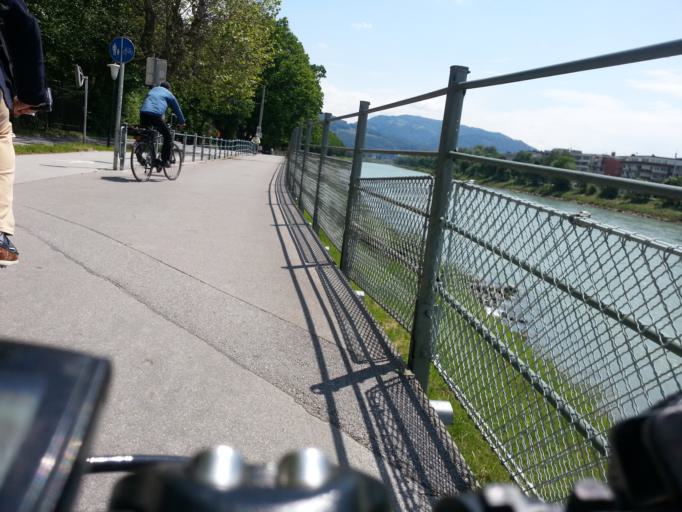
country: AT
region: Salzburg
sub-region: Salzburg Stadt
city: Salzburg
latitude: 47.7983
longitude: 13.0550
